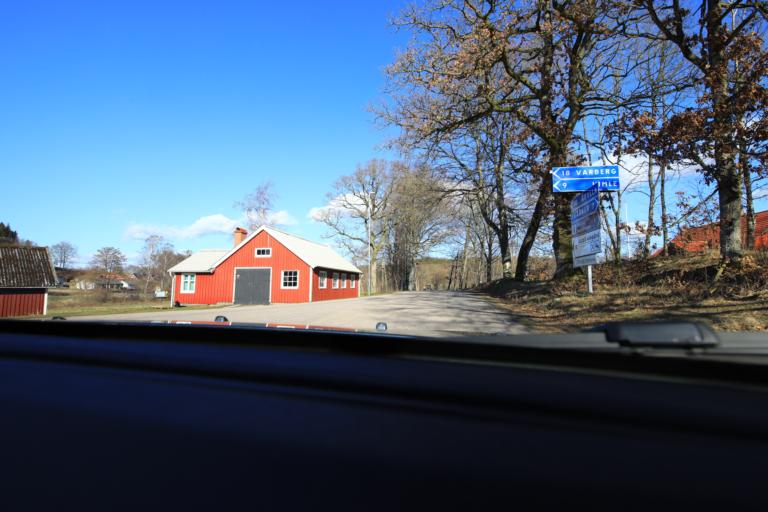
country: SE
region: Halland
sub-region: Varbergs Kommun
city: Tvaaker
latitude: 57.0667
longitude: 12.4884
